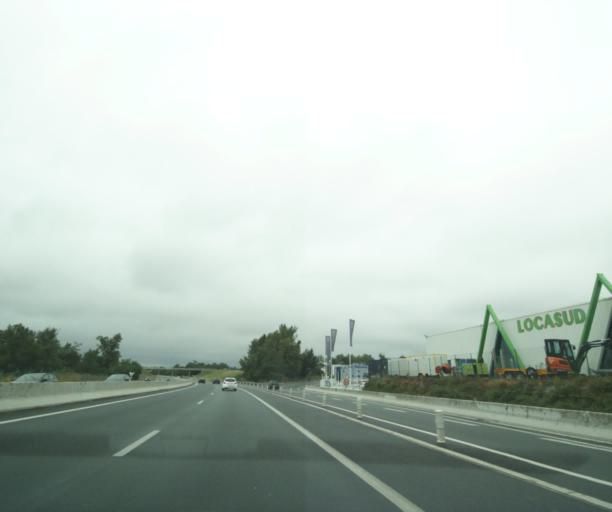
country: FR
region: Midi-Pyrenees
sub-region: Departement du Tarn
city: Albi
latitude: 43.9283
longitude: 2.1739
